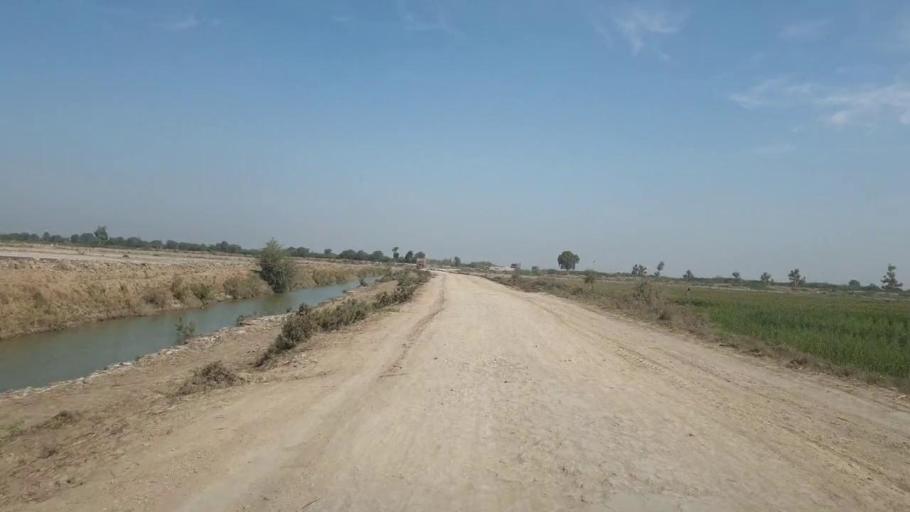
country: PK
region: Sindh
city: Samaro
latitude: 25.3170
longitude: 69.2319
